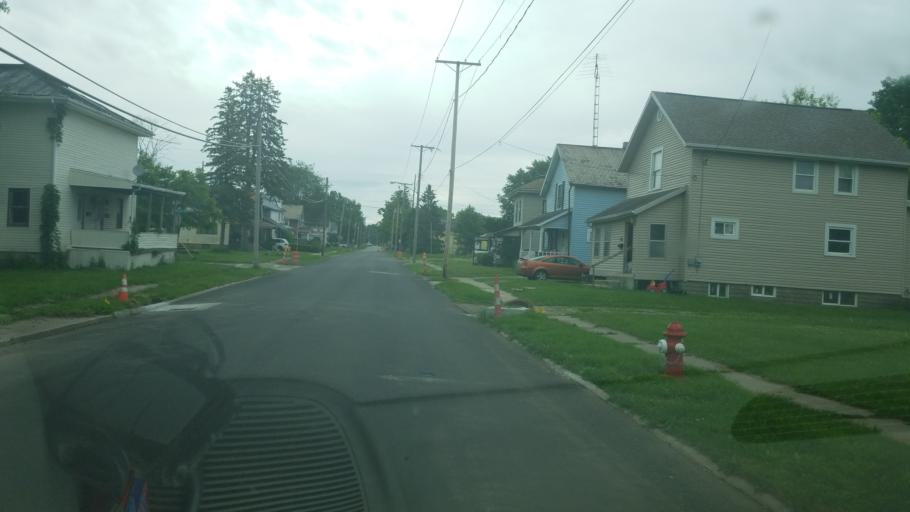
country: US
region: Ohio
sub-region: Crawford County
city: Bucyrus
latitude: 40.8050
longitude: -82.9650
